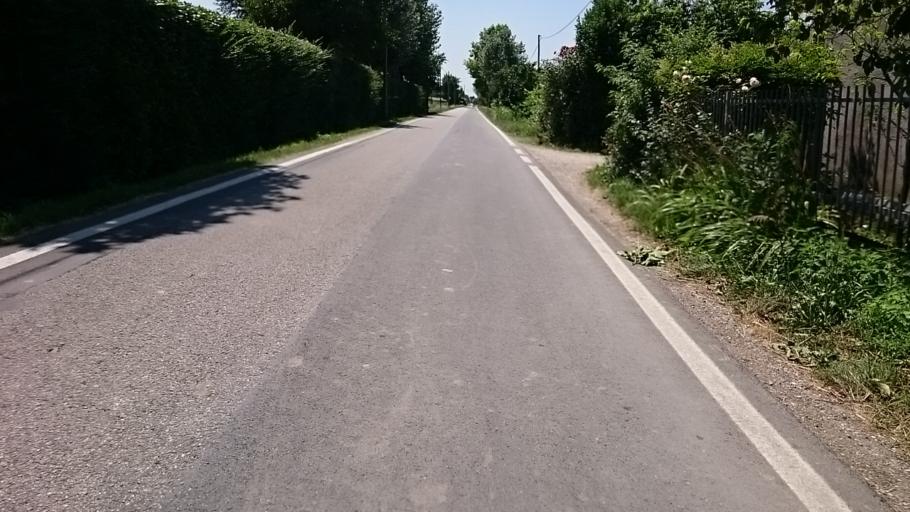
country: IT
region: Veneto
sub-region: Provincia di Venezia
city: Sant'Angelo
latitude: 45.5111
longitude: 11.9948
